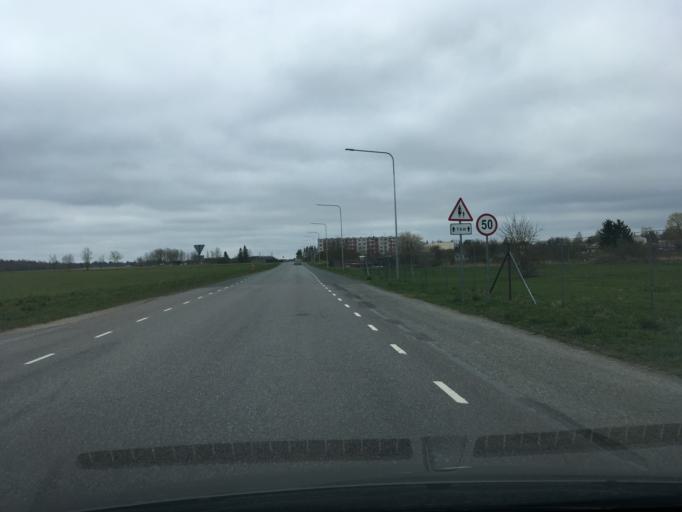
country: EE
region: Harju
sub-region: Rae vald
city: Vaida
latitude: 59.2917
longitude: 24.9768
